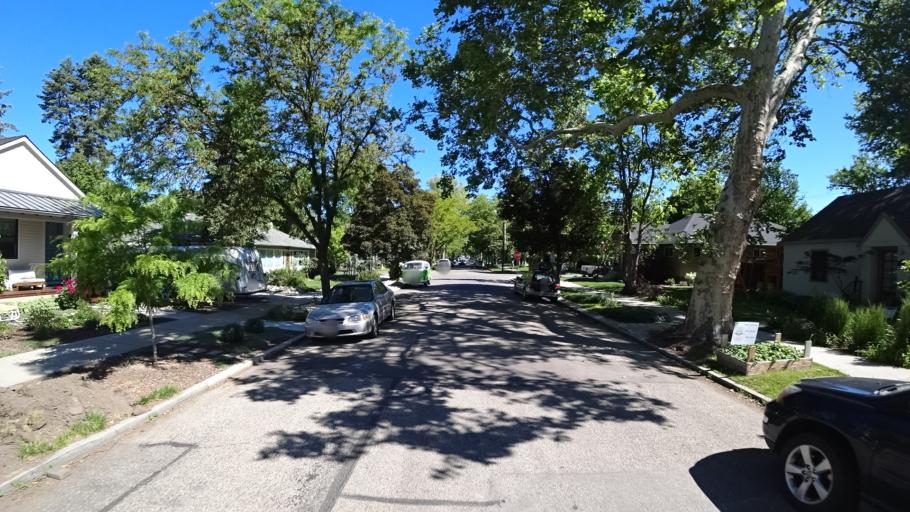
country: US
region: Idaho
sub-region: Ada County
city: Boise
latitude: 43.6335
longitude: -116.2134
